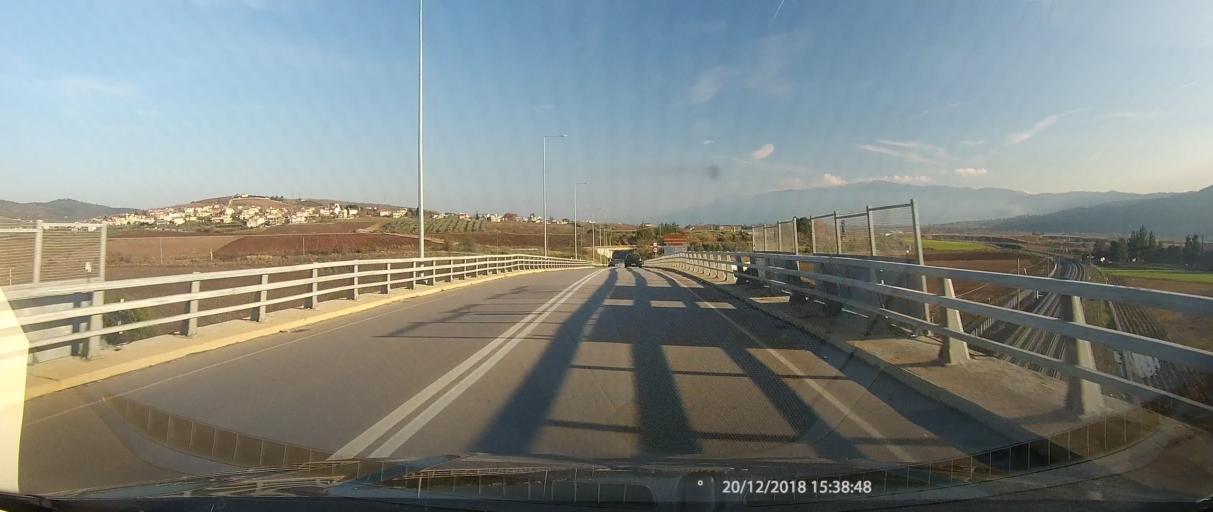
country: GR
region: Central Greece
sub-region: Nomos Fthiotidos
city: Stavros
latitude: 38.9012
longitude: 22.3557
